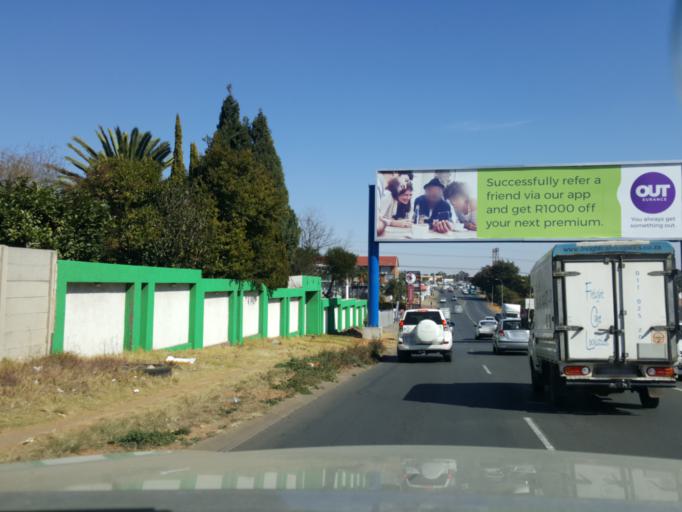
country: ZA
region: Gauteng
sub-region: City of Johannesburg Metropolitan Municipality
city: Modderfontein
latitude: -26.1336
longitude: 28.1977
